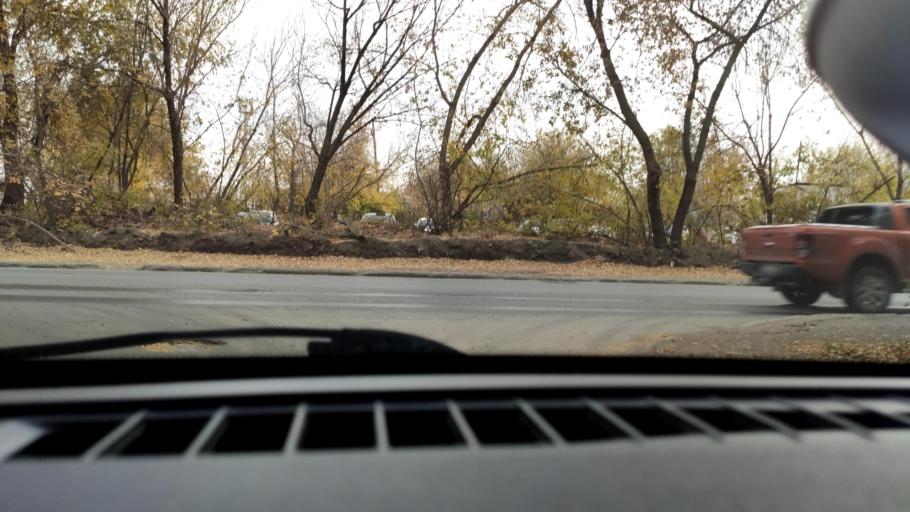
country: RU
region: Samara
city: Samara
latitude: 53.2249
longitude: 50.2102
